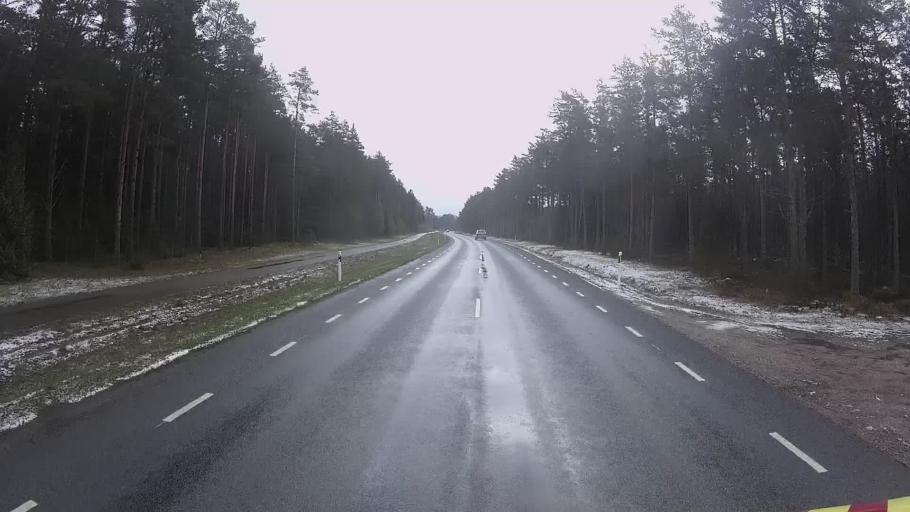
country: EE
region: Hiiumaa
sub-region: Kaerdla linn
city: Kardla
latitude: 58.9973
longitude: 22.7099
